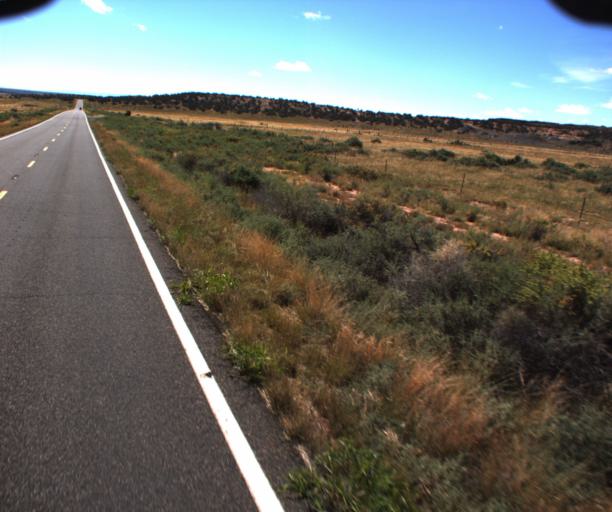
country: US
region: Arizona
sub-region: Apache County
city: Saint Johns
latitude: 34.7460
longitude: -109.2475
